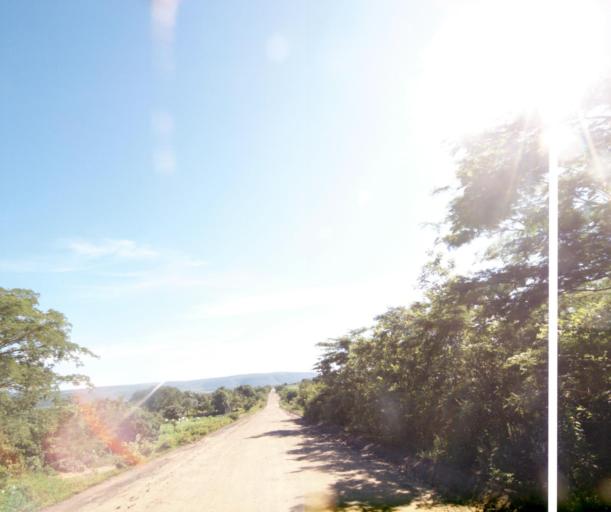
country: BR
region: Bahia
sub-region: Sao Felix Do Coribe
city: Santa Maria da Vitoria
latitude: -13.6251
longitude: -44.4200
